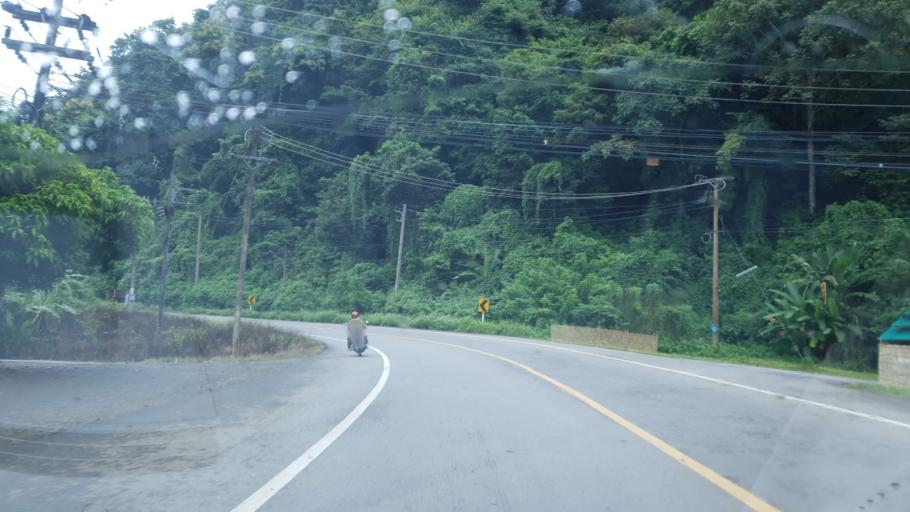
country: TH
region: Mae Hong Son
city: Ban Huai I Huak
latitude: 18.1641
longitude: 97.9553
